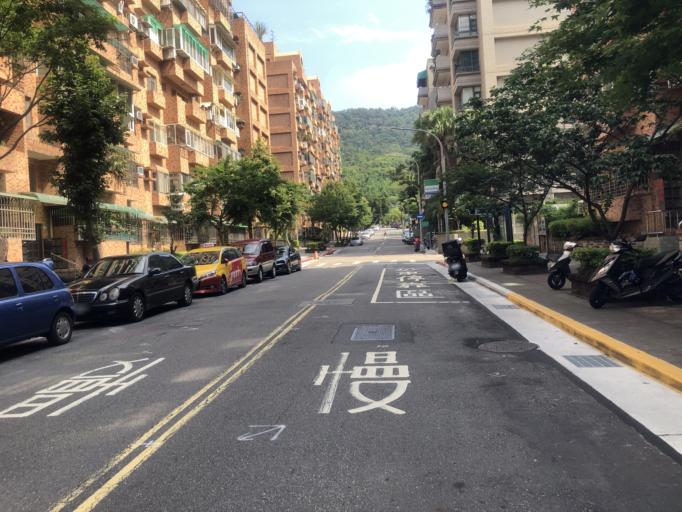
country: TW
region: Taipei
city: Taipei
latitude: 25.0838
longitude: 121.5380
